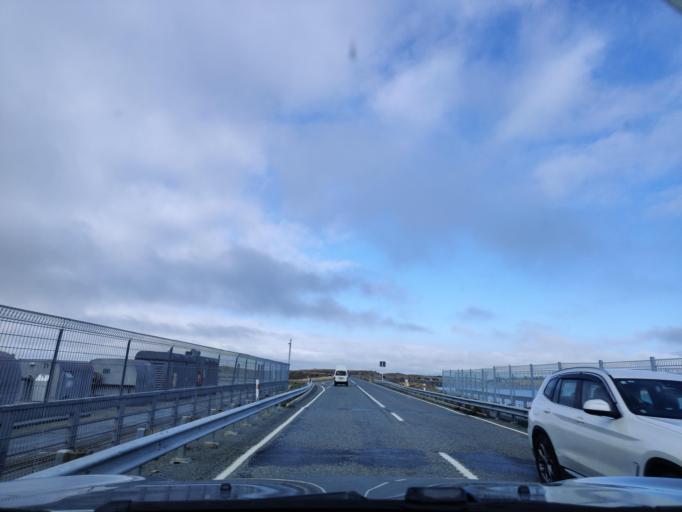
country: NZ
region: Canterbury
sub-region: Timaru District
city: Pleasant Point
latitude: -44.1879
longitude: 170.1494
